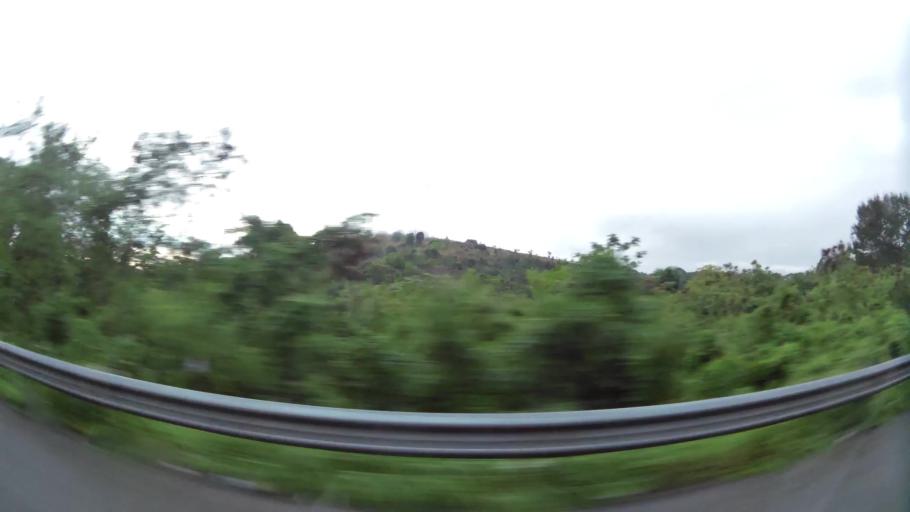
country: DO
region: San Cristobal
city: Villa Altagracia
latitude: 18.6056
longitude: -70.1383
